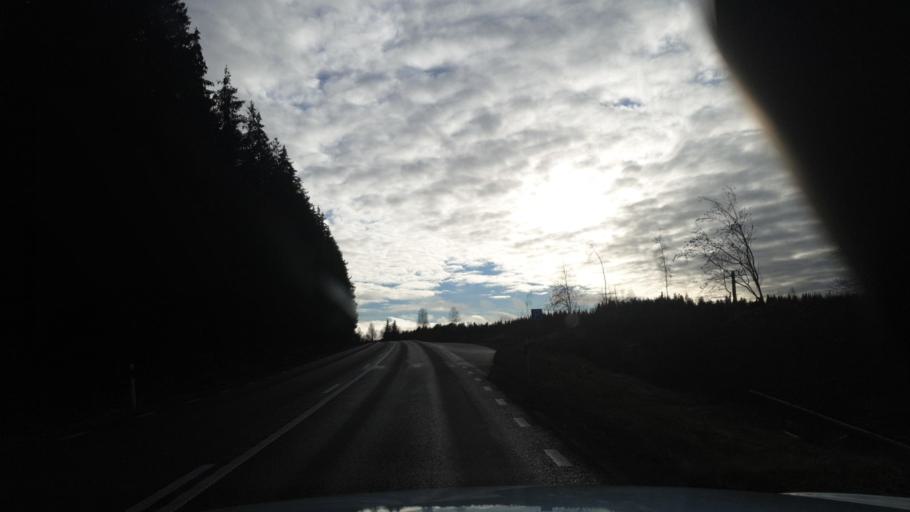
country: SE
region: Vaermland
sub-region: Sunne Kommun
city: Sunne
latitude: 59.6304
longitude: 12.9508
